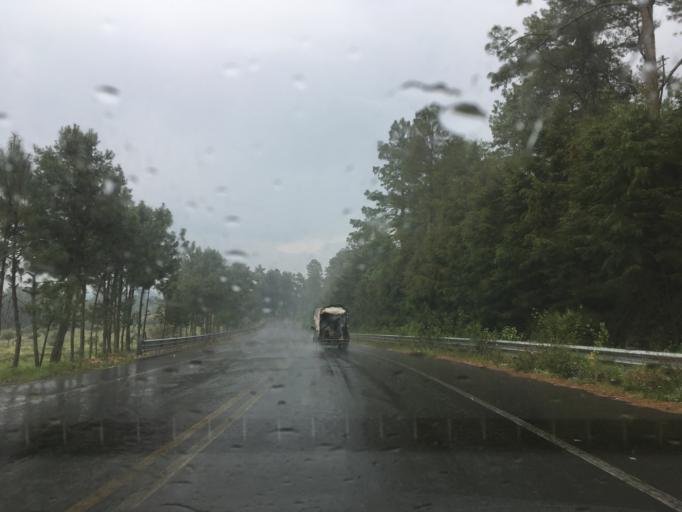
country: MX
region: Michoacan
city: Angahuan
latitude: 19.5682
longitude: -102.2751
